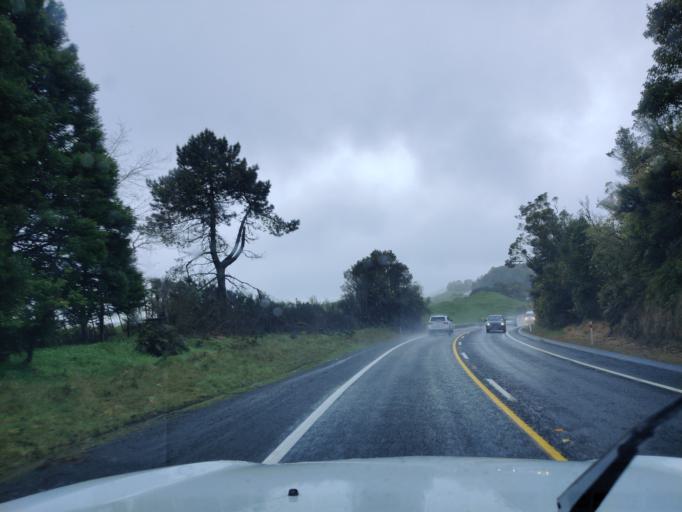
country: NZ
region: Waikato
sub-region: South Waikato District
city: Tokoroa
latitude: -38.0310
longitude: 175.9854
